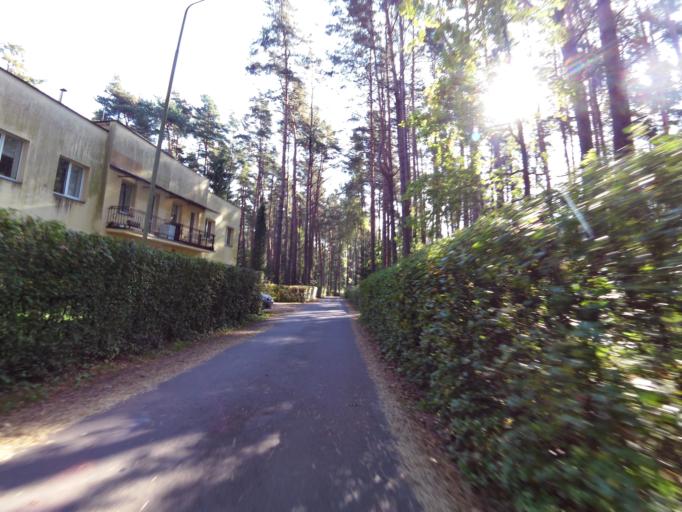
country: LT
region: Vilnius County
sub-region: Vilnius
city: Vilnius
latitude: 54.7344
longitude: 25.3030
